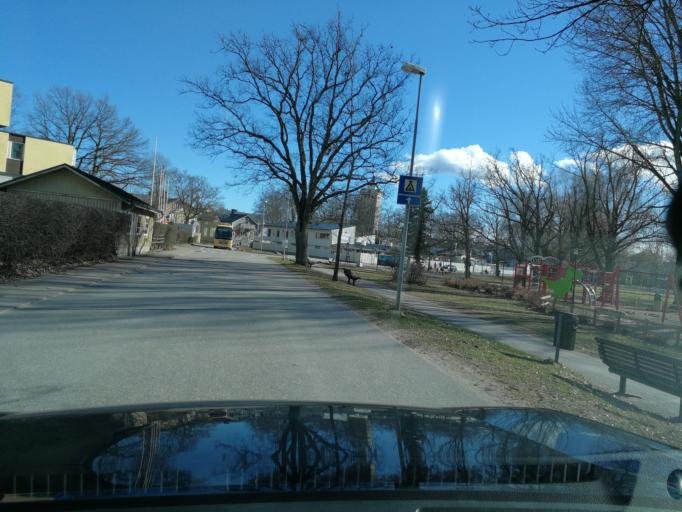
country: FI
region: Uusimaa
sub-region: Raaseporin
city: Ekenaes
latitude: 59.9763
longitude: 23.4326
